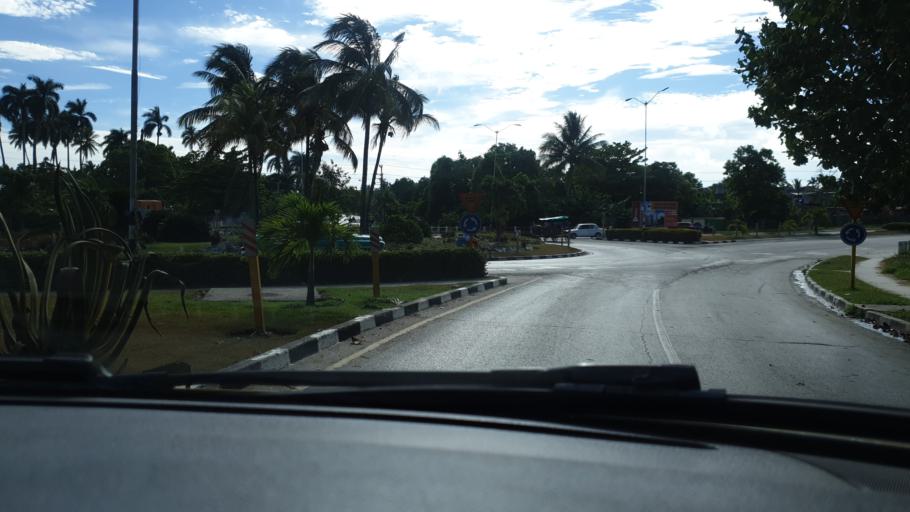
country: CU
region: Villa Clara
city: Santa Clara
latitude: 22.4155
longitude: -79.9465
